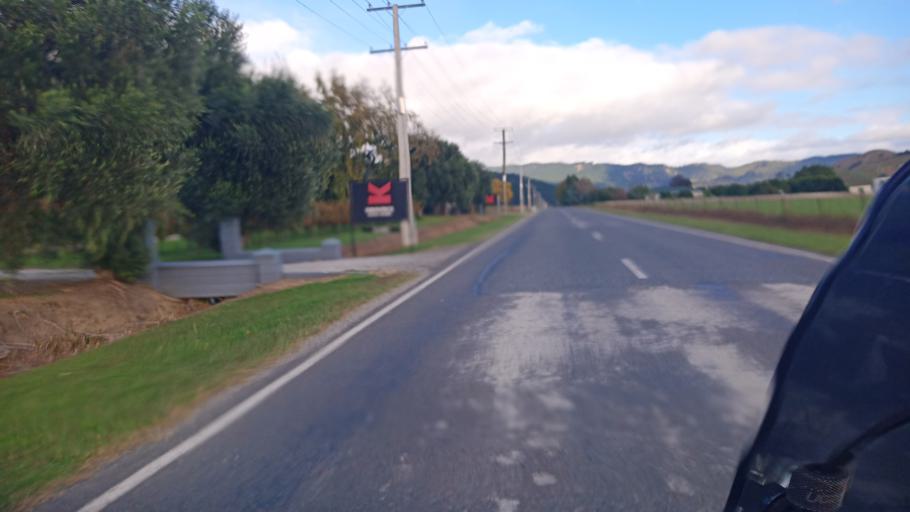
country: NZ
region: Gisborne
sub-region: Gisborne District
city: Gisborne
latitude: -38.6332
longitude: 177.8696
